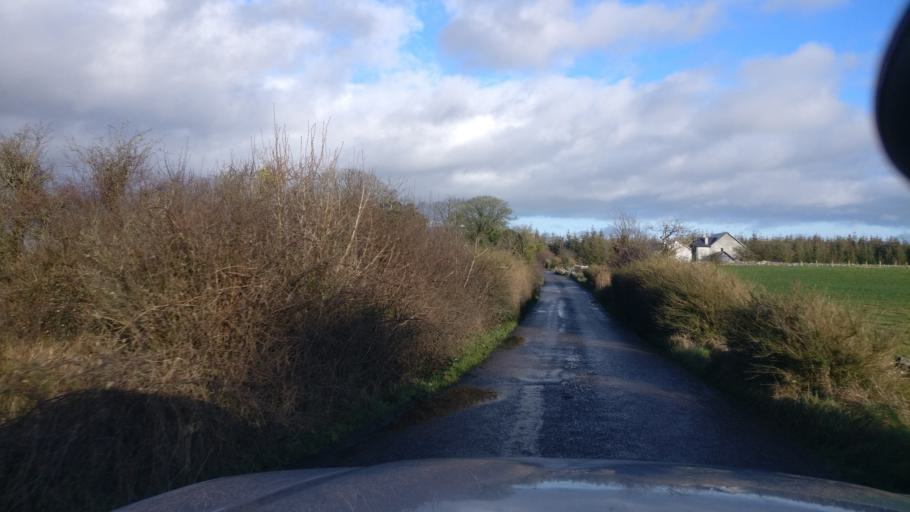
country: IE
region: Connaught
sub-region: County Galway
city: Loughrea
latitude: 53.2583
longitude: -8.6176
